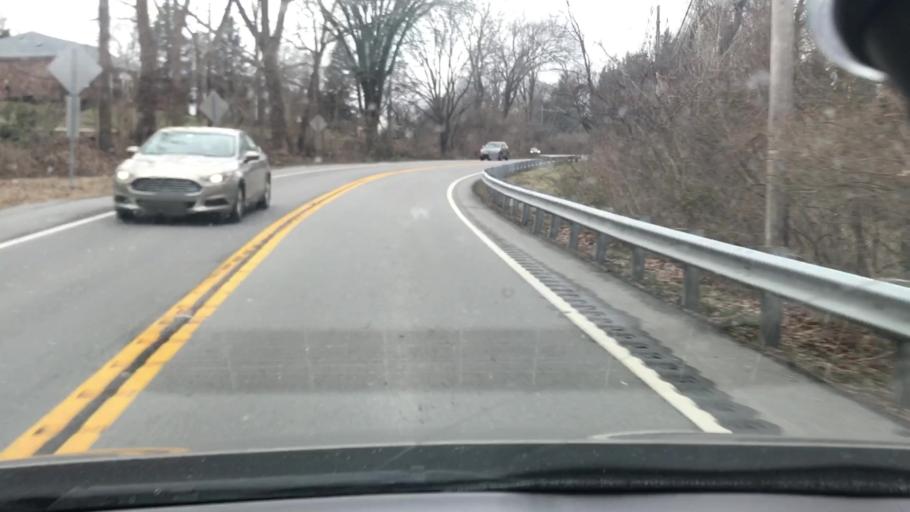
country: US
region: Kentucky
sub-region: Jefferson County
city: Barbourmeade
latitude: 38.2922
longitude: -85.6124
